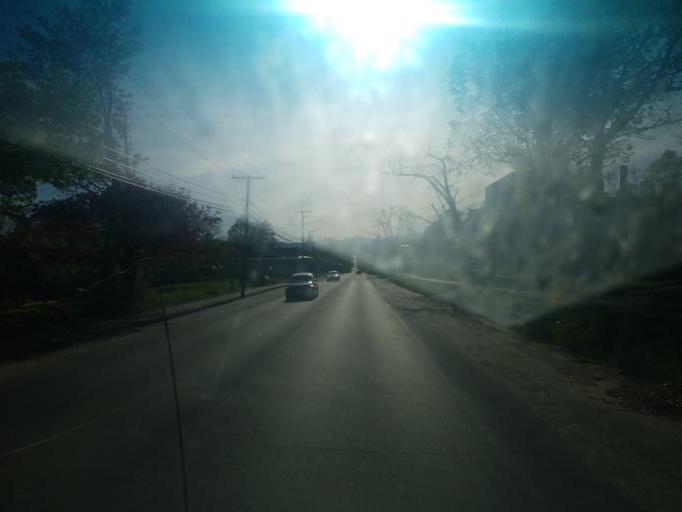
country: US
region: New Hampshire
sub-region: Grafton County
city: Littleton
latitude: 44.2800
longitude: -71.6926
